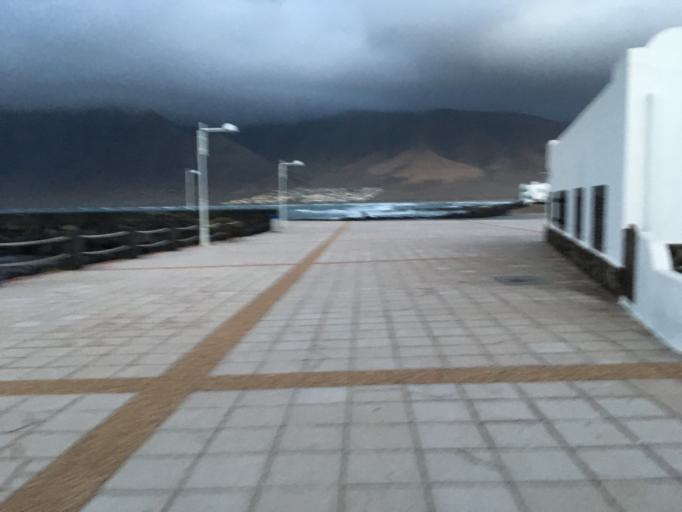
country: ES
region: Canary Islands
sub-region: Provincia de Las Palmas
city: Teguise
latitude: 29.1199
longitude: -13.5664
